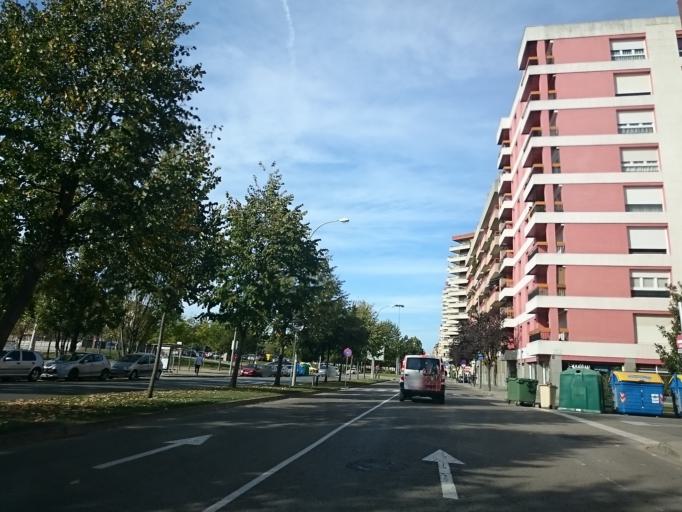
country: ES
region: Catalonia
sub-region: Provincia de Barcelona
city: Vic
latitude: 41.9272
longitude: 2.2491
